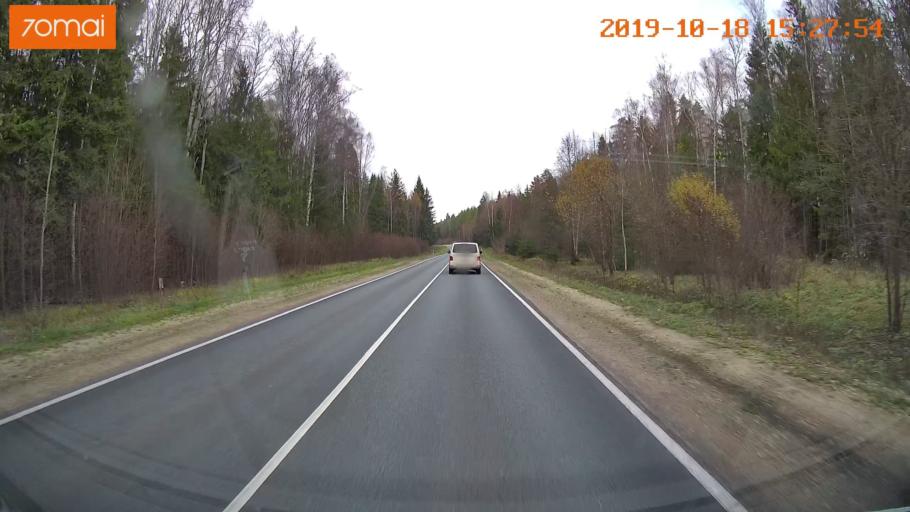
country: RU
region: Vladimir
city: Anopino
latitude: 55.7594
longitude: 40.6727
